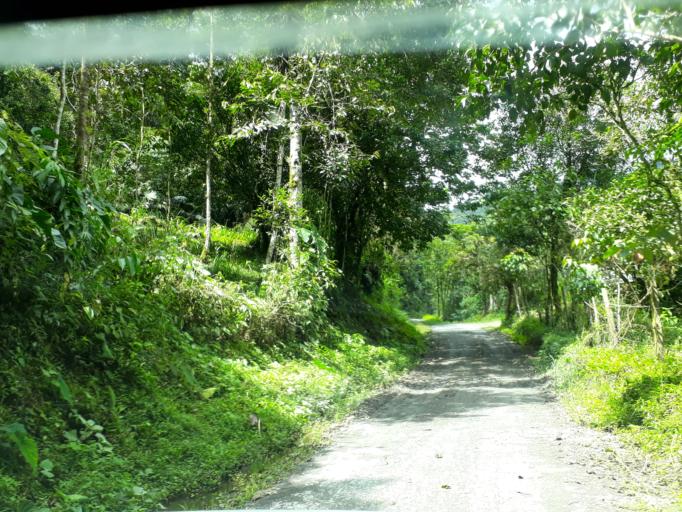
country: CO
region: Cundinamarca
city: Topaipi
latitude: 5.3067
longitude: -74.1978
